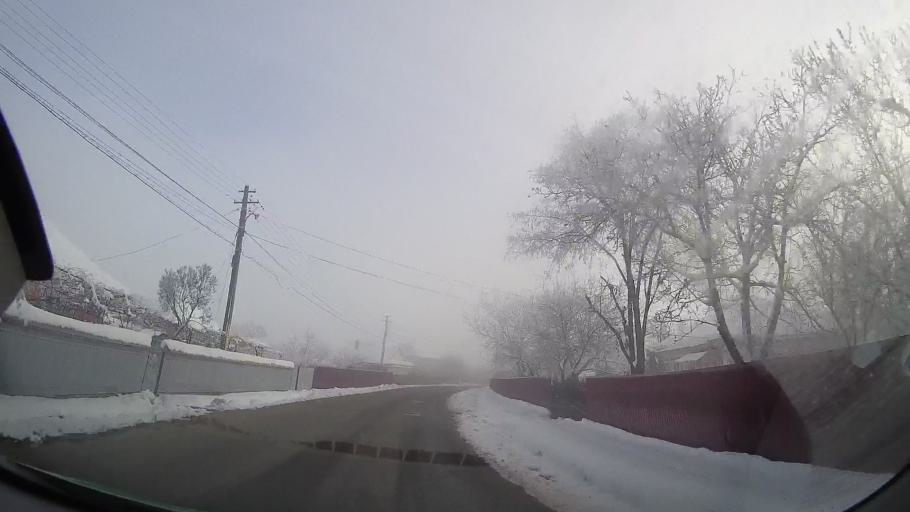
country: RO
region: Iasi
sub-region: Comuna Valea Seaca
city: Topile
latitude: 47.2420
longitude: 26.6670
